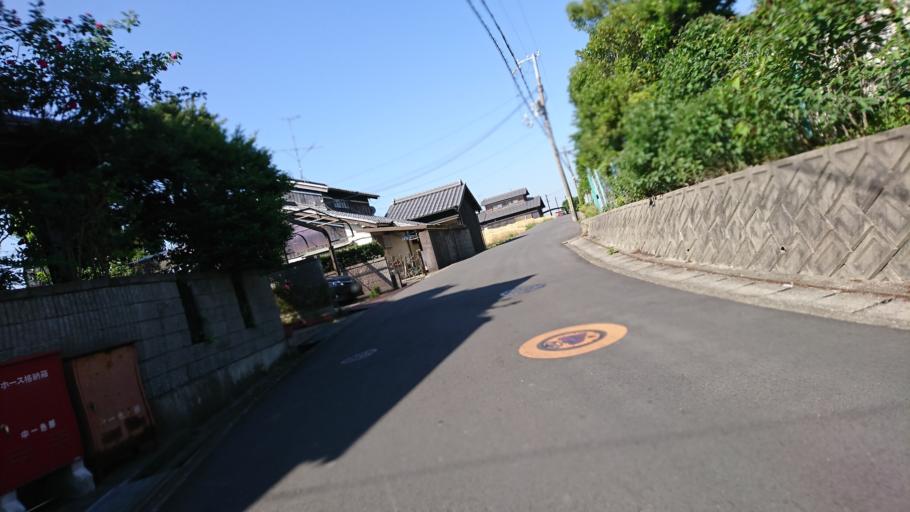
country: JP
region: Hyogo
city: Kakogawacho-honmachi
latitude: 34.7614
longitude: 134.8837
